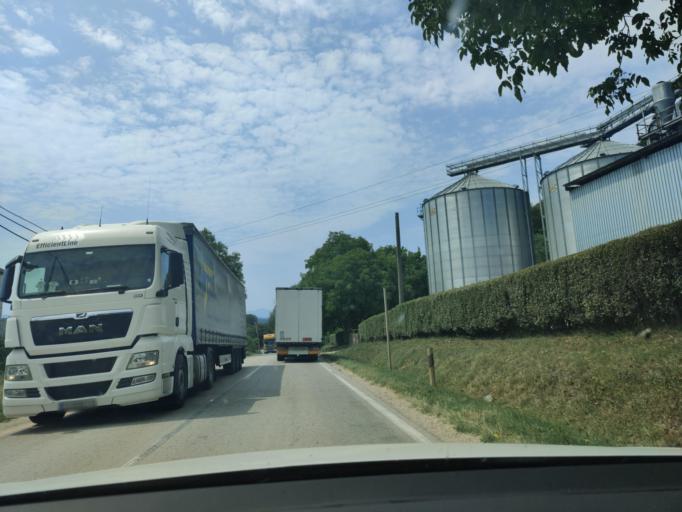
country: BG
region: Vidin
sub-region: Obshtina Dimovo
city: Dimovo
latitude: 43.7495
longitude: 22.7366
